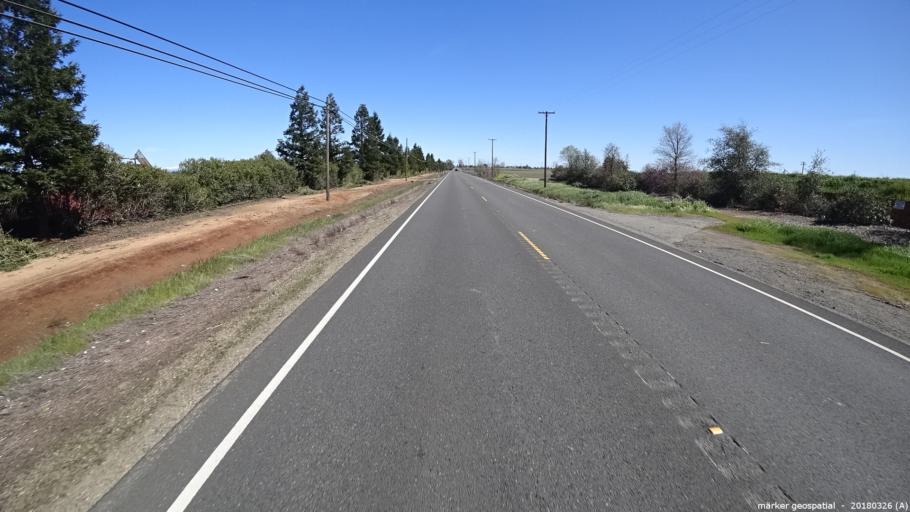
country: US
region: California
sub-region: Sacramento County
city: Rosemont
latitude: 38.5252
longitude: -121.3208
